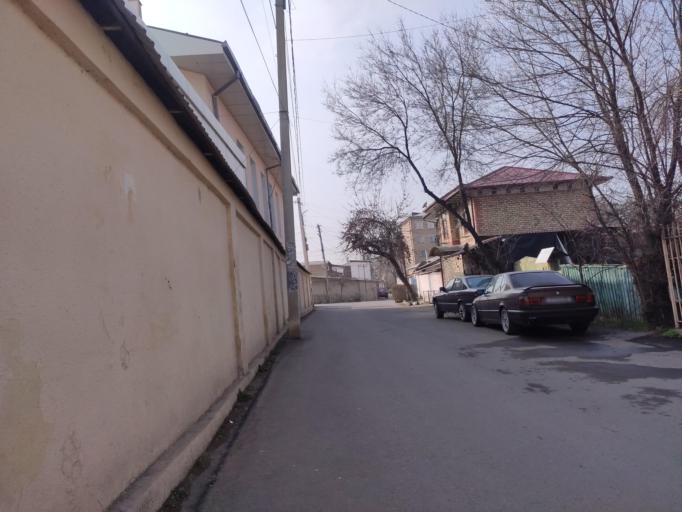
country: UZ
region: Toshkent Shahri
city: Tashkent
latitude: 41.2726
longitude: 69.2749
